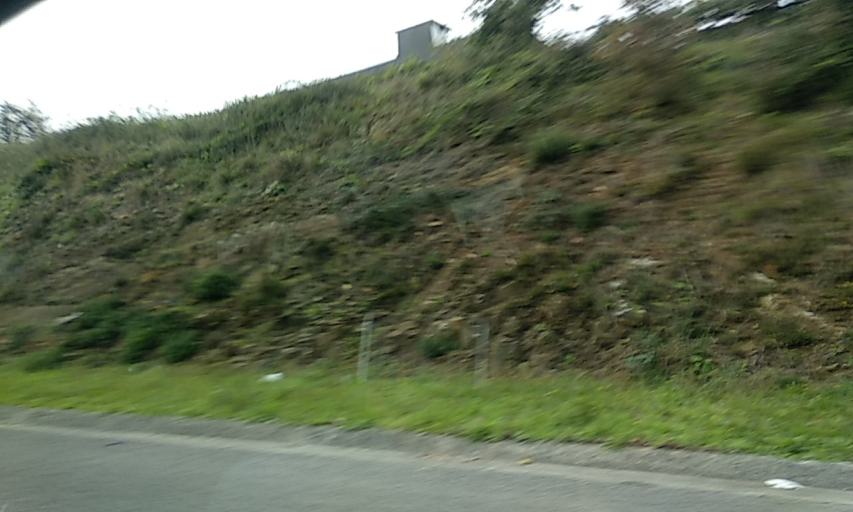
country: PT
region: Porto
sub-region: Santo Tirso
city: Santo Tirso
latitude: 41.3493
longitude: -8.5070
